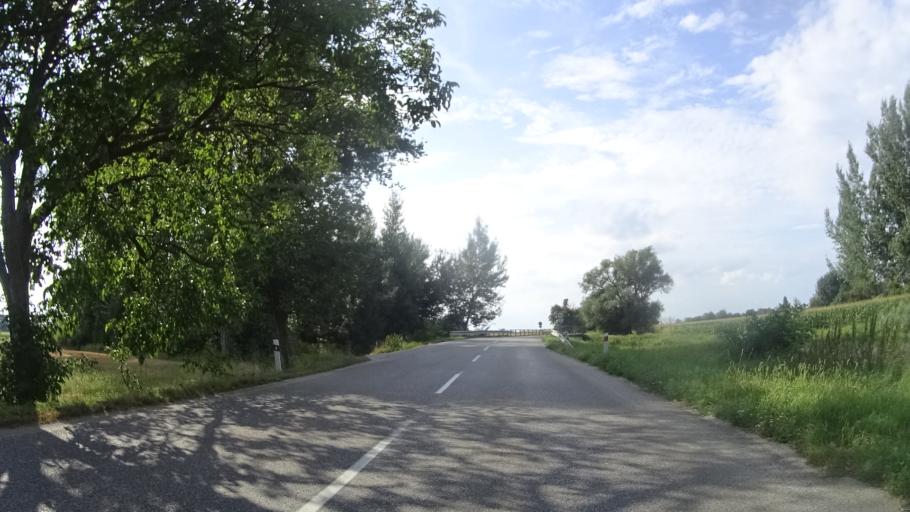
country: SK
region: Trnavsky
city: Gabcikovo
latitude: 47.9277
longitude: 17.4886
